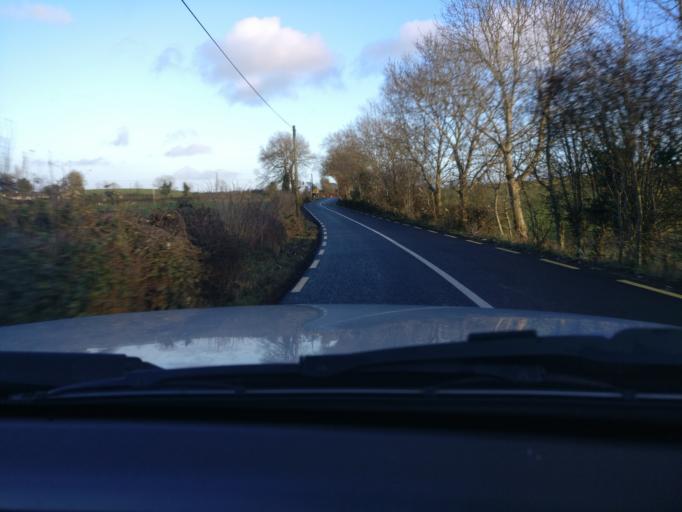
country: IE
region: Leinster
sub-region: An Mhi
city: Navan
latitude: 53.7960
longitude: -6.6977
